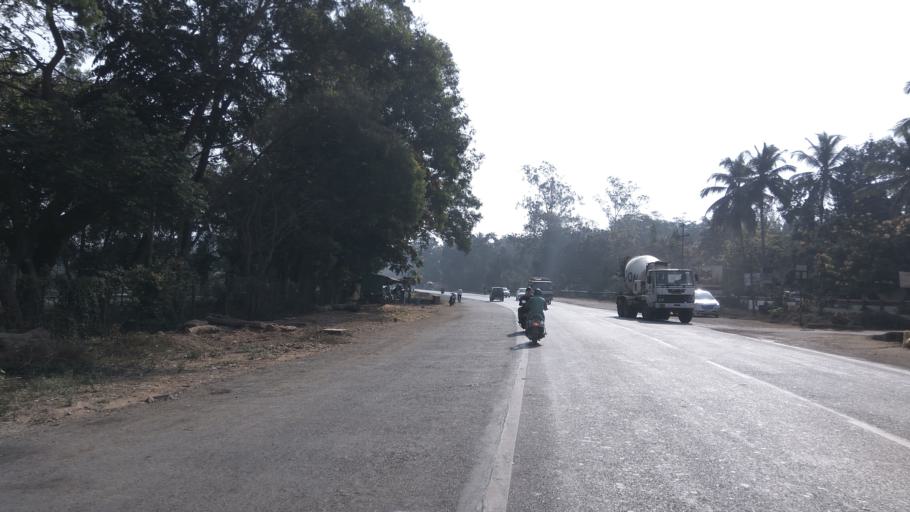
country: IN
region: Goa
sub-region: North Goa
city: Jua
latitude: 15.4933
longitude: 73.9410
